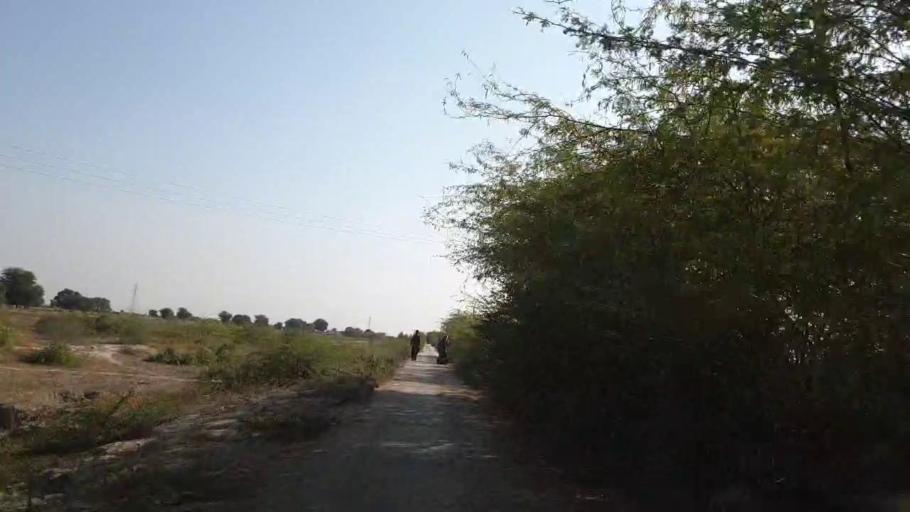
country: PK
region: Sindh
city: Nabisar
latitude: 25.0236
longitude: 69.4696
